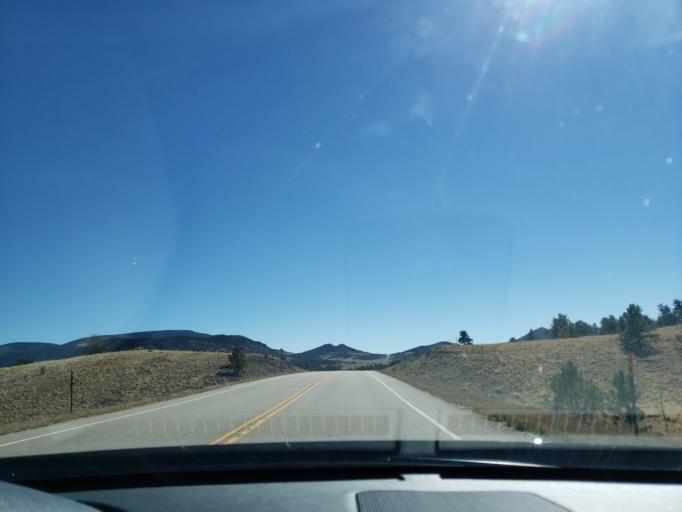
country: US
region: Colorado
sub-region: Chaffee County
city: Buena Vista
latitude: 38.8767
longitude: -105.6735
